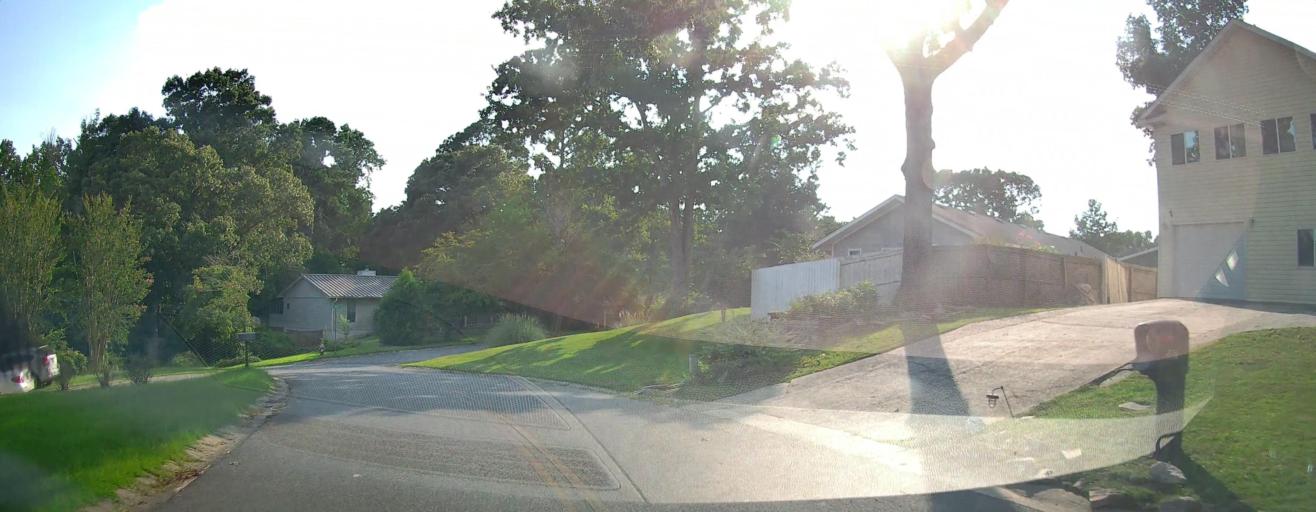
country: US
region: Georgia
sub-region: Houston County
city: Warner Robins
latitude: 32.5835
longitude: -83.6456
